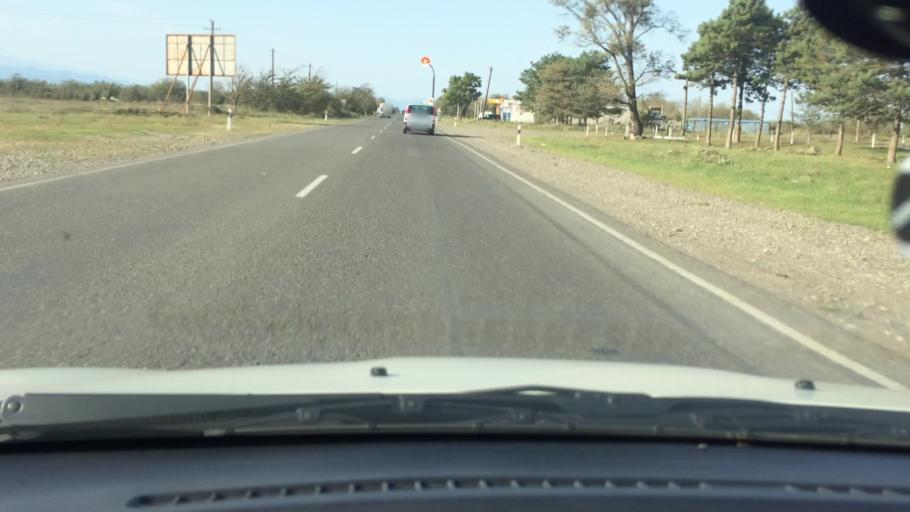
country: GE
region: Imereti
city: Kutaisi
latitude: 42.2265
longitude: 42.5931
